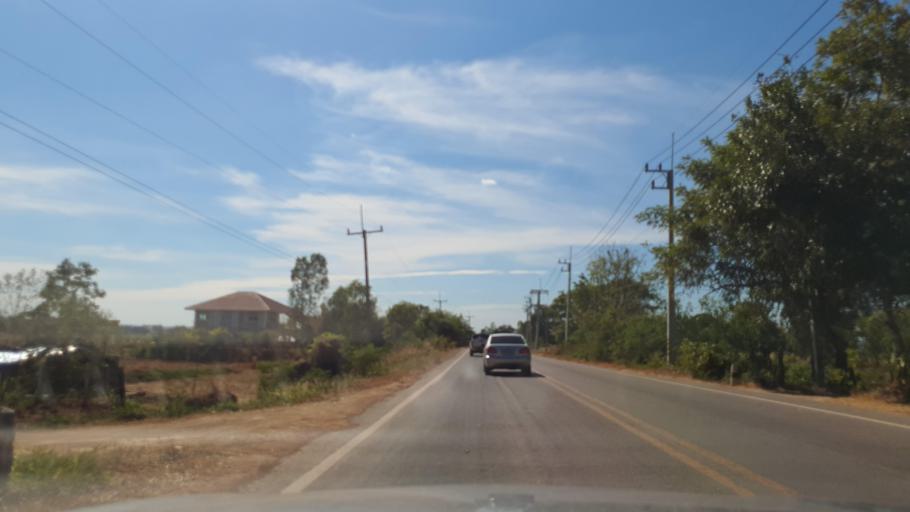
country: TH
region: Kalasin
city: Khao Wong
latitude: 16.7467
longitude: 104.1133
